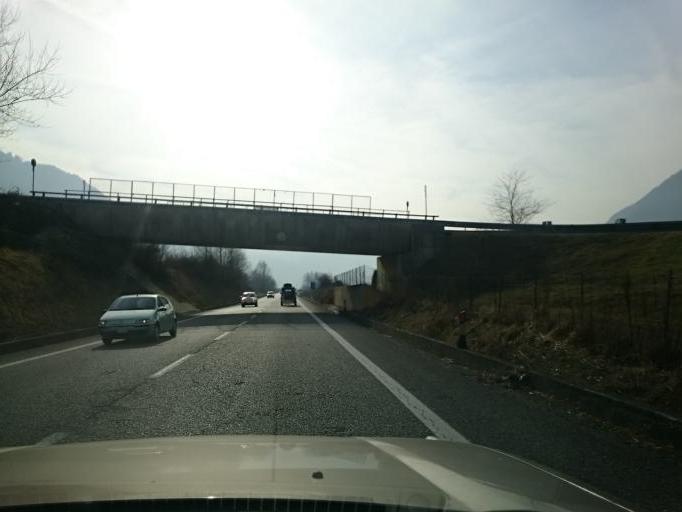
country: IT
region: Lombardy
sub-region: Provincia di Brescia
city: Niardo
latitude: 45.9755
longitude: 10.3234
